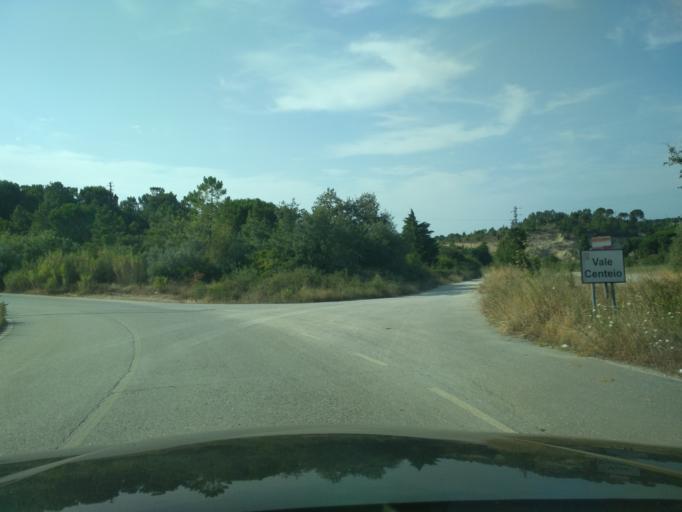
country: PT
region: Coimbra
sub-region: Condeixa-A-Nova
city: Condeixa-a-Nova
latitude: 40.1451
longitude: -8.4595
